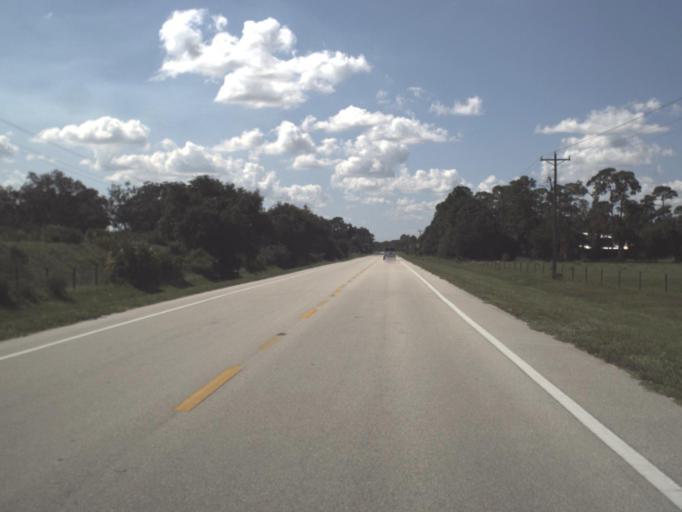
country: US
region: Florida
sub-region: Hendry County
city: Port LaBelle
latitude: 26.8160
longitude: -81.2921
